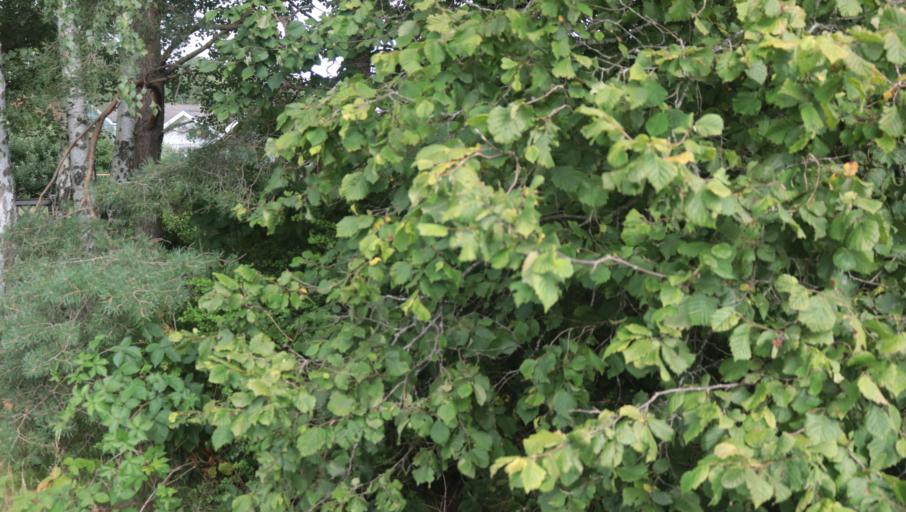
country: SE
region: Blekinge
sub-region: Karlshamns Kommun
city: Karlshamn
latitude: 56.2053
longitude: 14.8615
